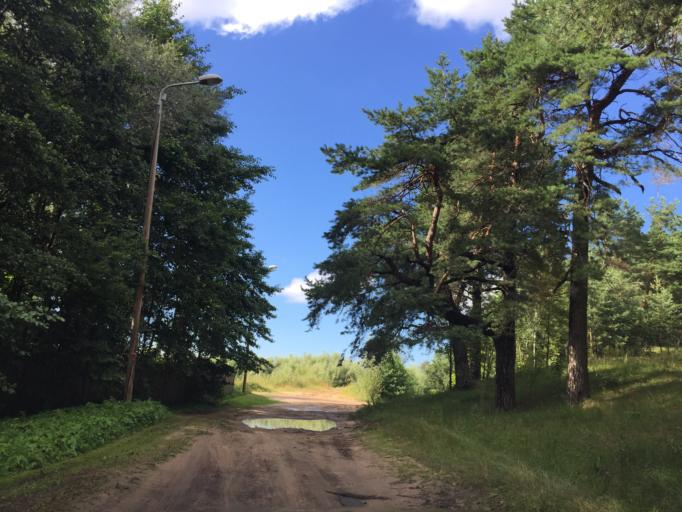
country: LV
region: Riga
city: Jaunciems
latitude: 57.0410
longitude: 24.1711
